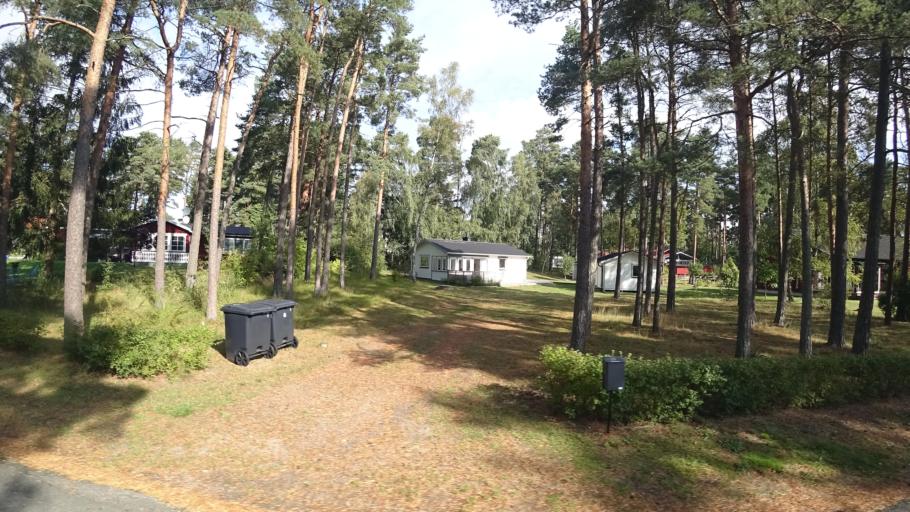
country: SE
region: Skane
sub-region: Kristianstads Kommun
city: Ahus
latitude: 55.9390
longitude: 14.2959
